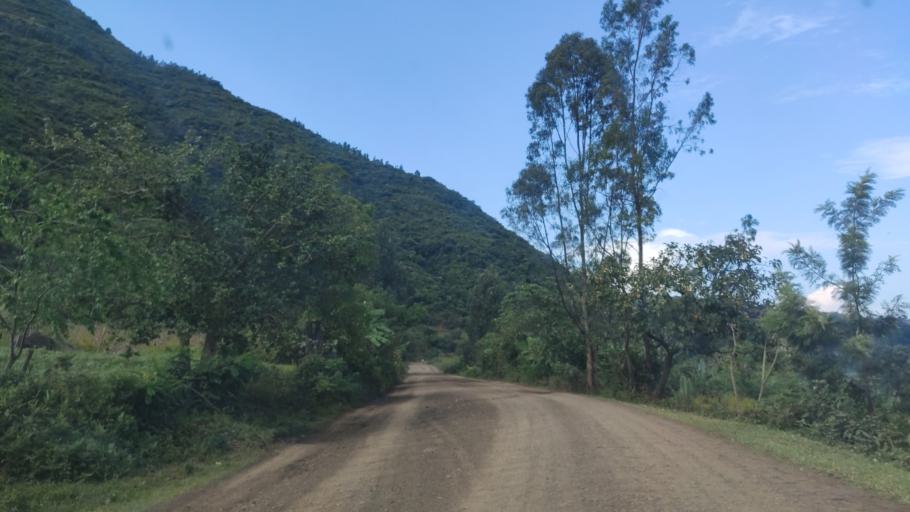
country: ET
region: Southern Nations, Nationalities, and People's Region
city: Arba Minch'
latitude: 6.4399
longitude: 37.3914
